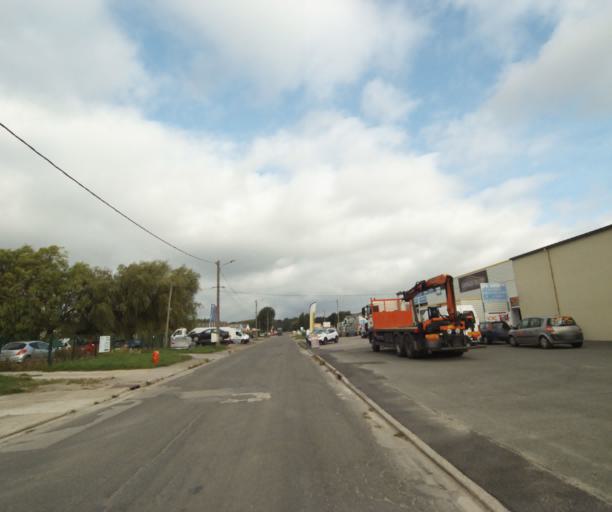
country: FR
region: Nord-Pas-de-Calais
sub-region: Departement du Pas-de-Calais
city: Etaples
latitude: 50.5191
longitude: 1.6628
